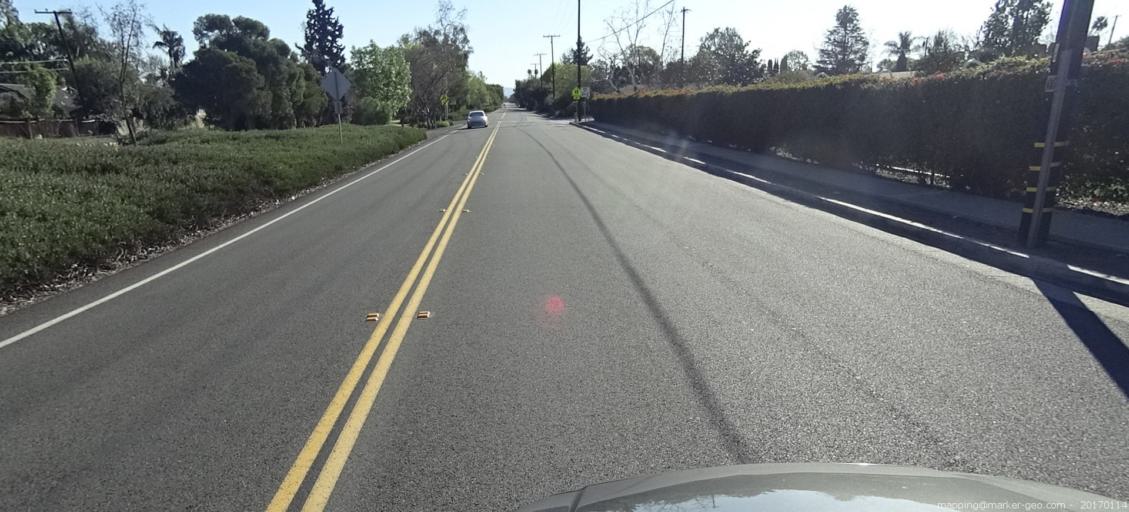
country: US
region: California
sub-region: Orange County
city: North Tustin
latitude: 33.7728
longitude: -117.8110
